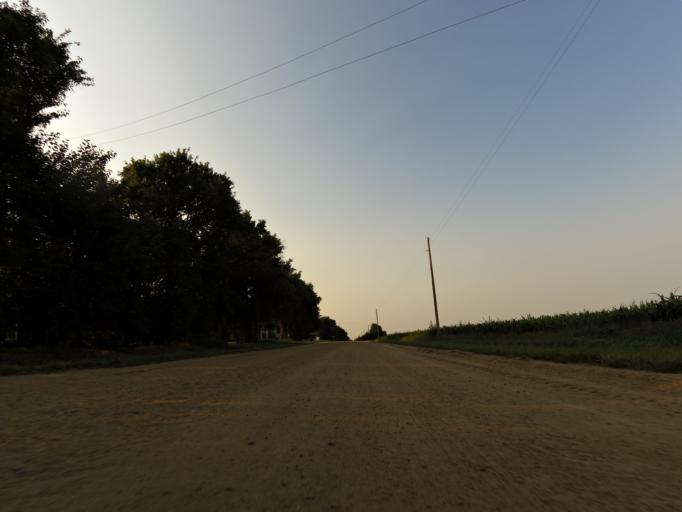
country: US
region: Kansas
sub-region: Reno County
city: South Hutchinson
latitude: 37.9920
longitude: -97.9956
